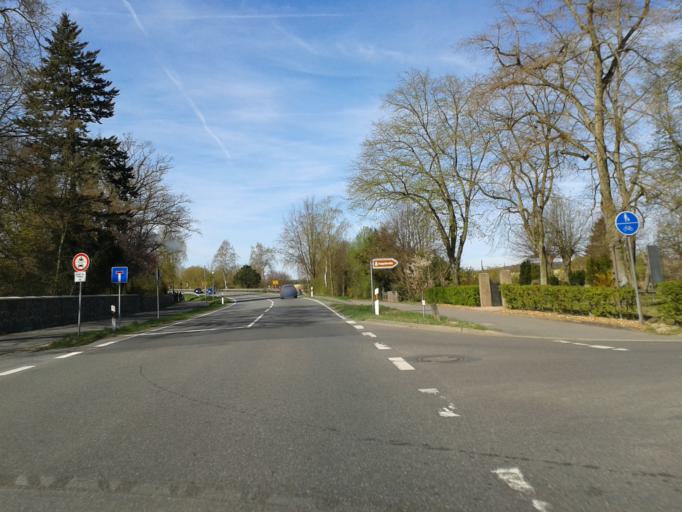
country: DE
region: Lower Saxony
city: Uelzen
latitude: 52.9567
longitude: 10.5427
